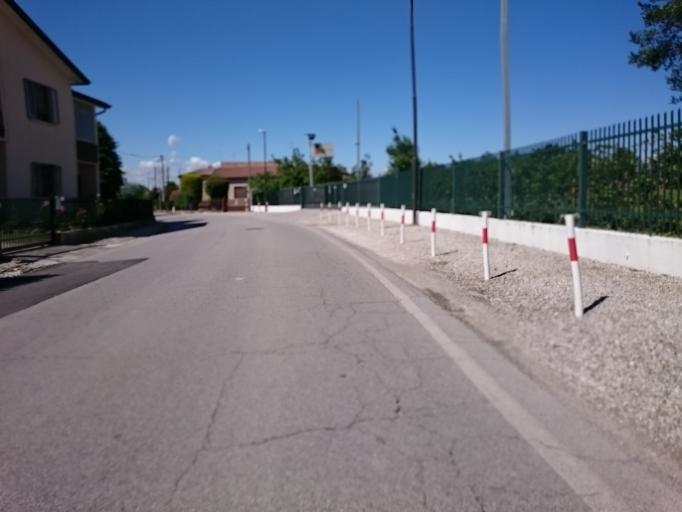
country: IT
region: Veneto
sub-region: Provincia di Padova
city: Arzergrande
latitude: 45.2764
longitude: 12.0438
